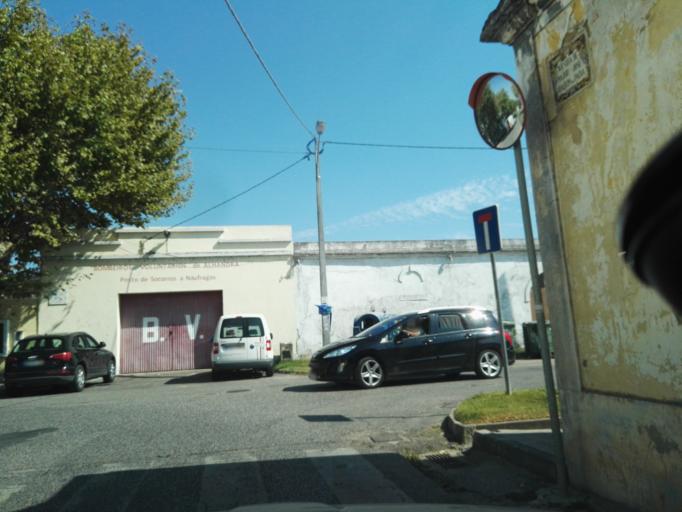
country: PT
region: Lisbon
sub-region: Vila Franca de Xira
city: Alhandra
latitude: 38.9247
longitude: -9.0068
